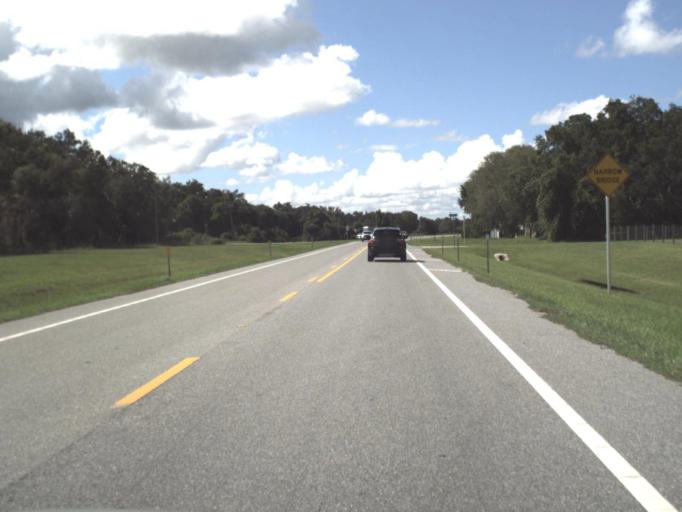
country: US
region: Florida
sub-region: Sarasota County
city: Lake Sarasota
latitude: 27.3418
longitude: -82.1520
